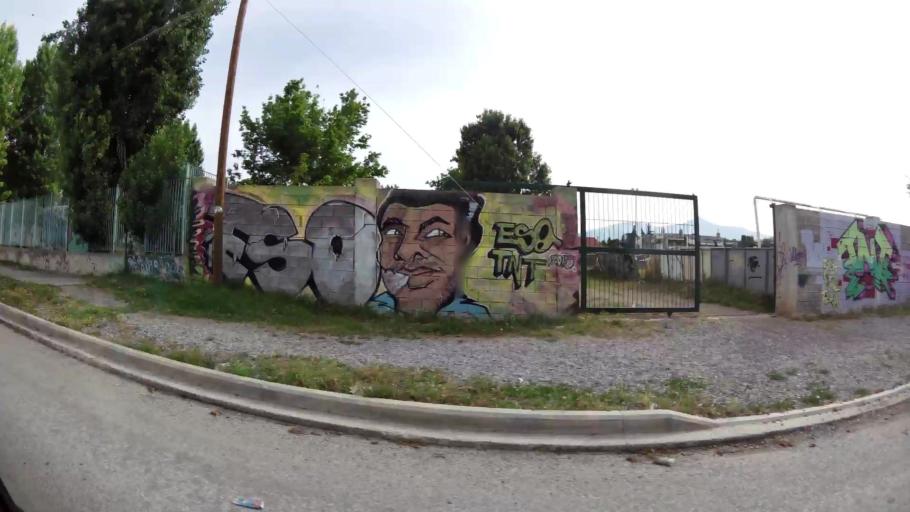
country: GR
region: Central Macedonia
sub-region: Nomos Thessalonikis
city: Thermi
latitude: 40.5476
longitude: 23.0134
